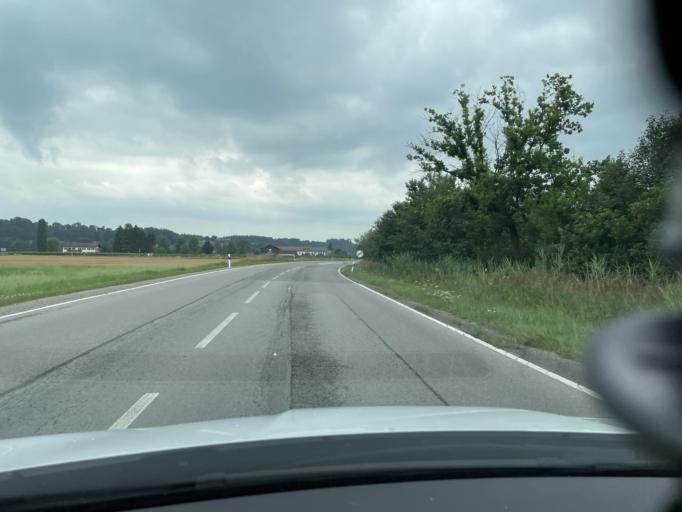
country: DE
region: Bavaria
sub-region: Upper Bavaria
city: Ramerberg
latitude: 47.9878
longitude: 12.1464
